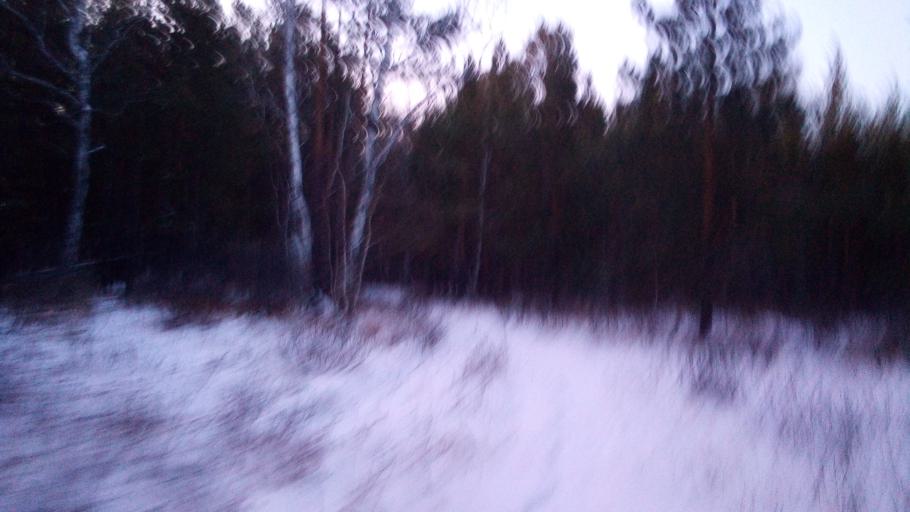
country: RU
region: Chelyabinsk
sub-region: Gorod Chelyabinsk
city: Chelyabinsk
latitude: 55.1630
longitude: 61.3330
